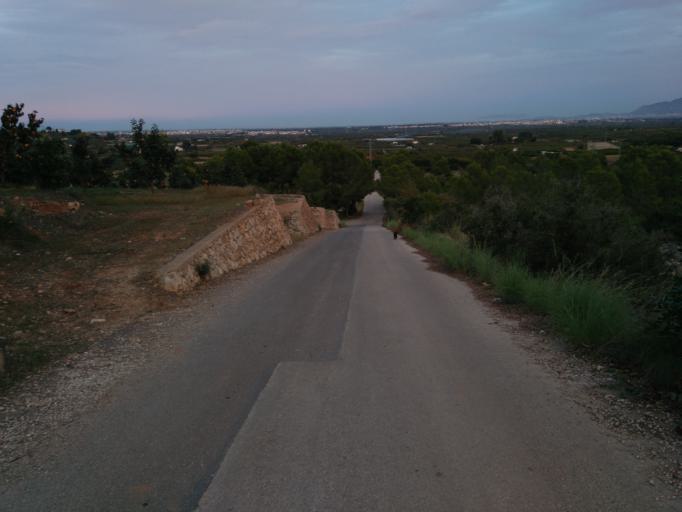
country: ES
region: Valencia
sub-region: Provincia de Valencia
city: Benimodo
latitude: 39.2006
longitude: -0.5774
